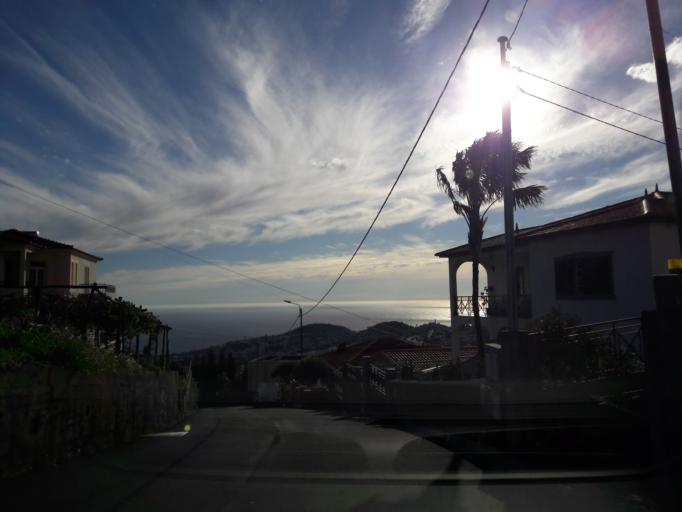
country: PT
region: Madeira
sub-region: Funchal
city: Nossa Senhora do Monte
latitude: 32.6751
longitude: -16.9207
